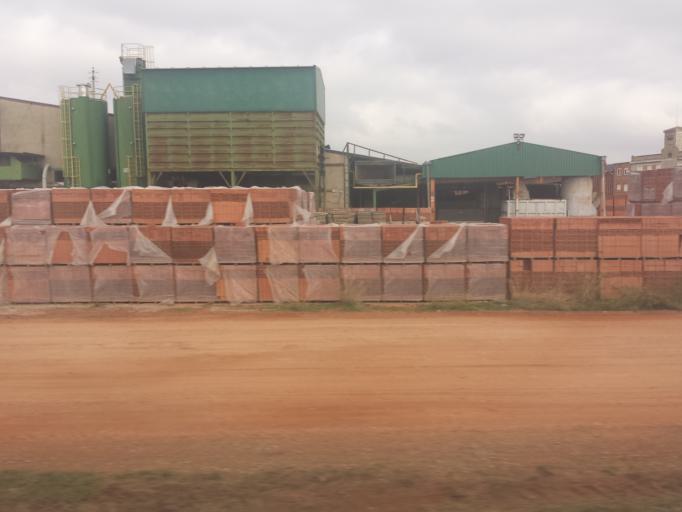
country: ES
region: Aragon
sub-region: Provincia de Zaragoza
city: Alagon
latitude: 41.7732
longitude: -1.1153
